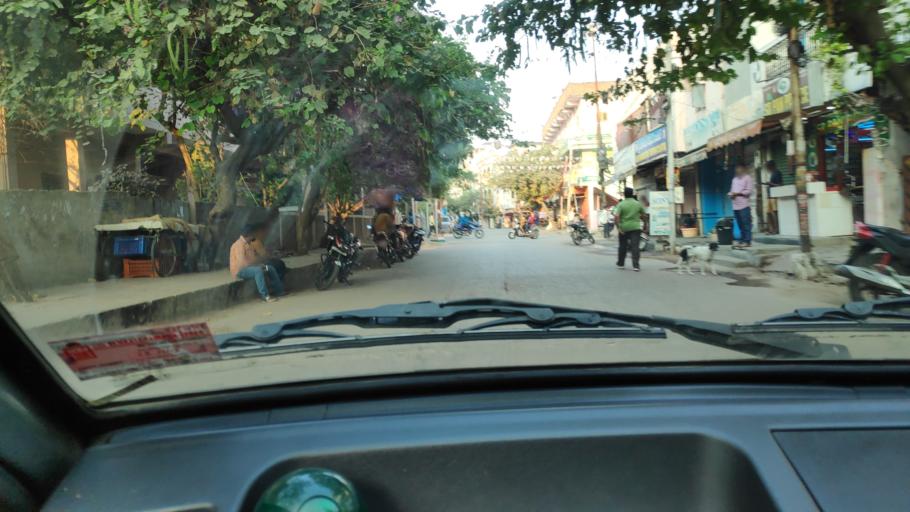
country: IN
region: Telangana
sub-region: Rangareddi
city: Gaddi Annaram
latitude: 17.3625
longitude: 78.5266
